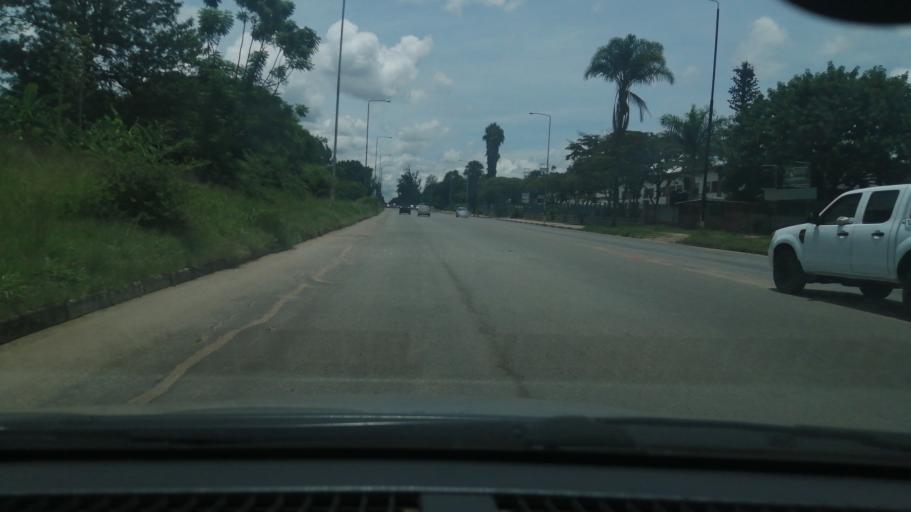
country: ZW
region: Harare
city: Harare
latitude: -17.8824
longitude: 31.0704
